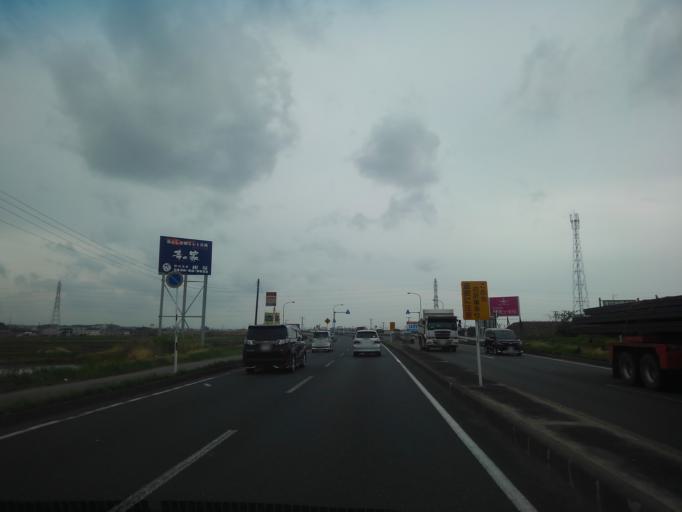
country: JP
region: Chiba
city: Kisarazu
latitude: 35.4052
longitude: 139.9437
